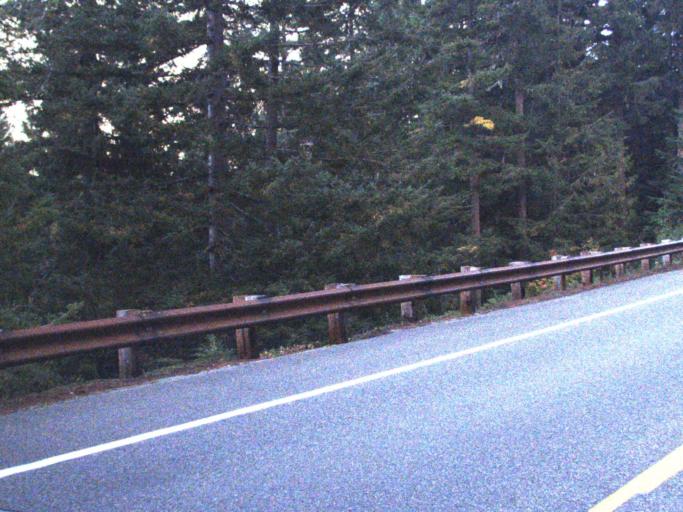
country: US
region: Washington
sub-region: Snohomish County
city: Darrington
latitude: 48.7257
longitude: -121.0332
